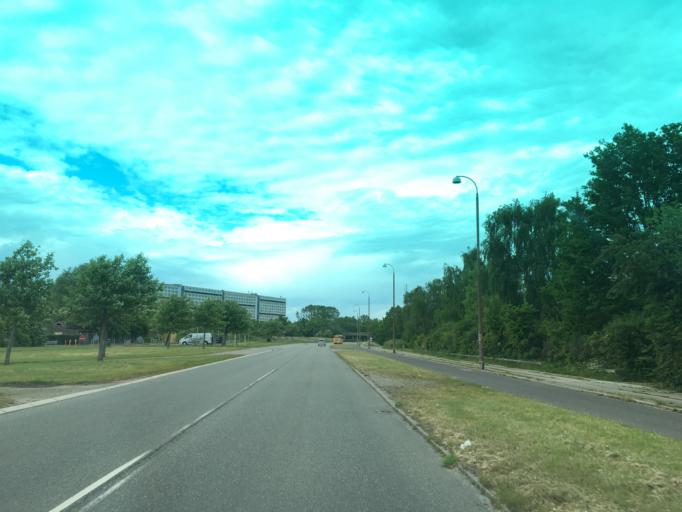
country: DK
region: Capital Region
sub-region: Hvidovre Kommune
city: Hvidovre
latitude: 55.6227
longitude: 12.4594
